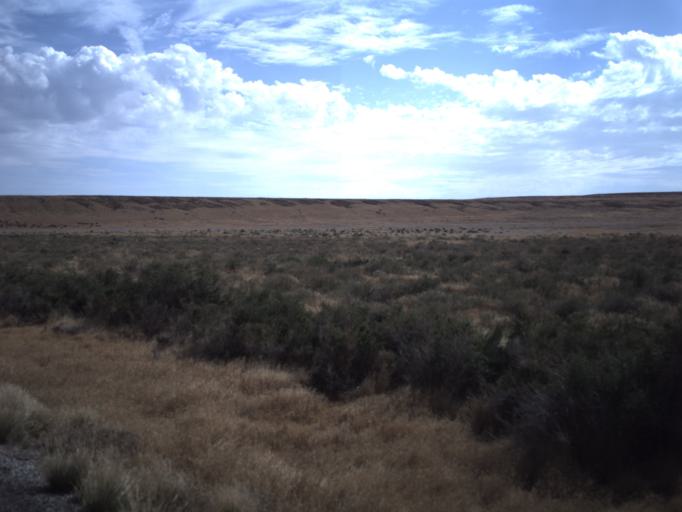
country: US
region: Utah
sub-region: Tooele County
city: Wendover
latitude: 41.4161
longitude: -113.9165
